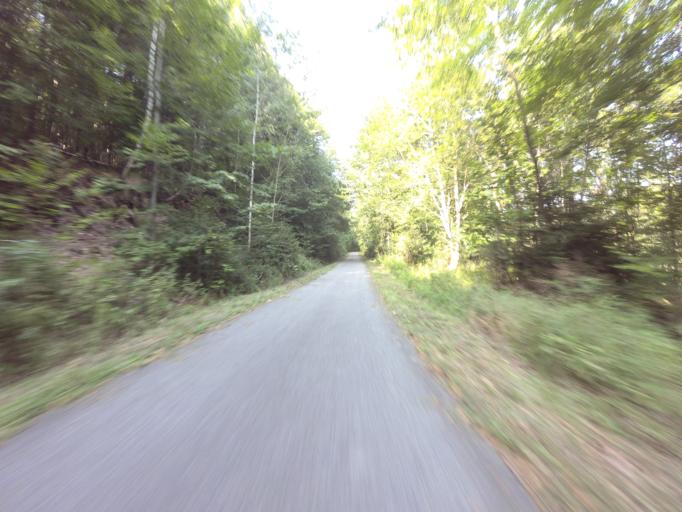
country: CZ
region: Jihocesky
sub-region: Okres Ceske Budejovice
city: Hluboka nad Vltavou
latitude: 49.0944
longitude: 14.4620
